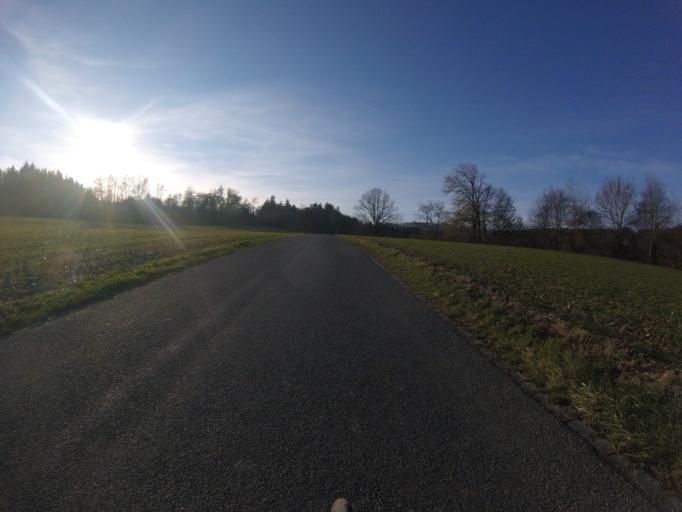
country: CH
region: Bern
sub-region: Bern-Mittelland District
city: Frauenkappelen
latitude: 46.9405
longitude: 7.3203
